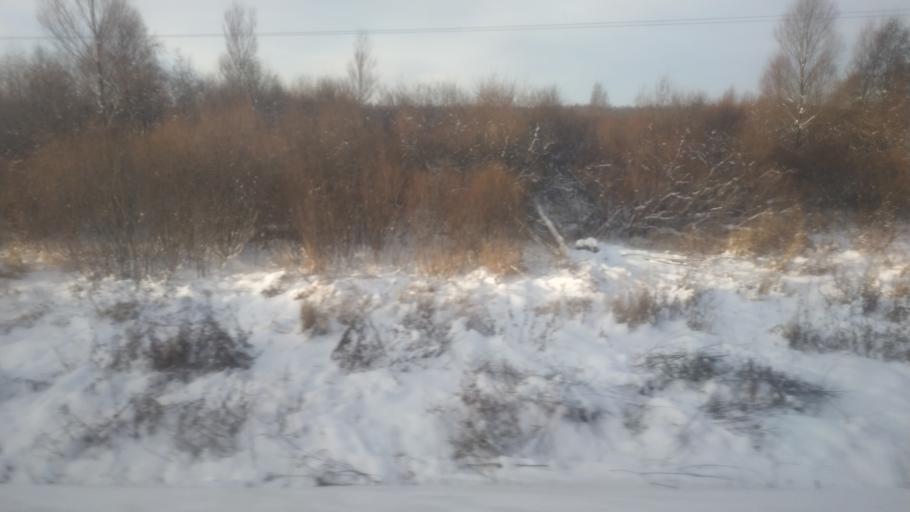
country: RU
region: Udmurtiya
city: Kizner
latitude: 56.2689
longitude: 51.4878
